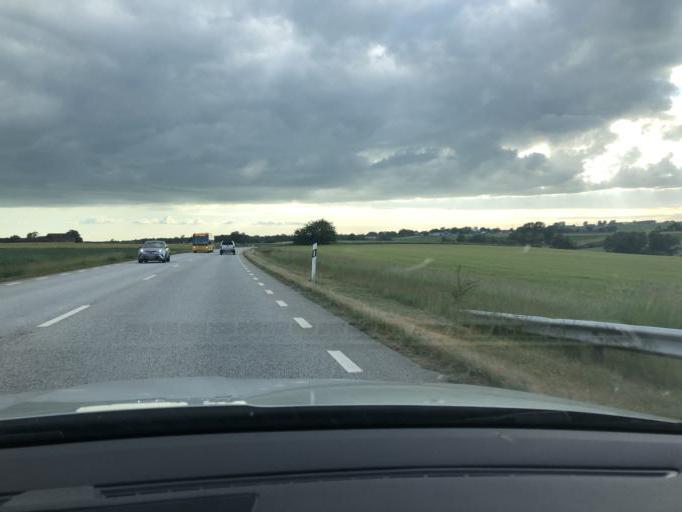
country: SE
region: Skane
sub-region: Simrishamns Kommun
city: Simrishamn
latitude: 55.5363
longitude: 14.3111
